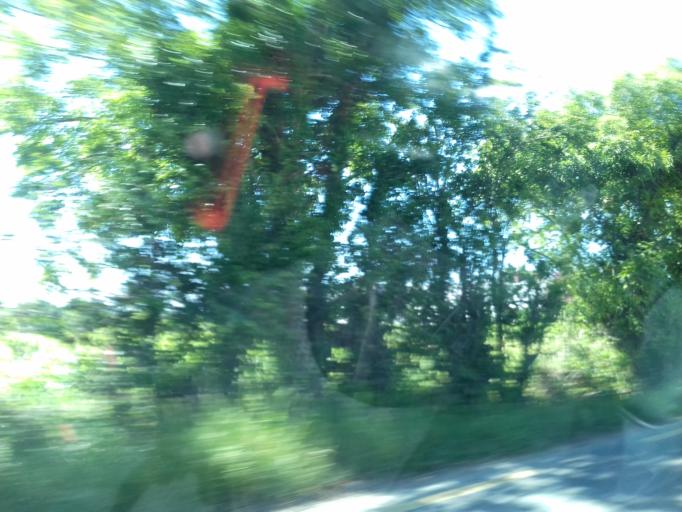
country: IE
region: Leinster
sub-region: An Mhi
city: Stamullin
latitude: 53.5529
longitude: -6.2723
